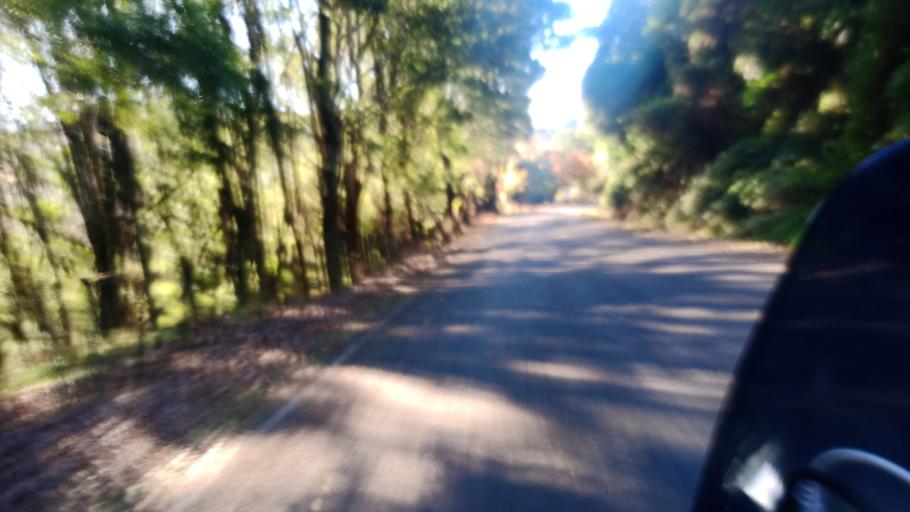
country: NZ
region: Hawke's Bay
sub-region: Wairoa District
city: Wairoa
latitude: -38.8187
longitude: 177.2925
